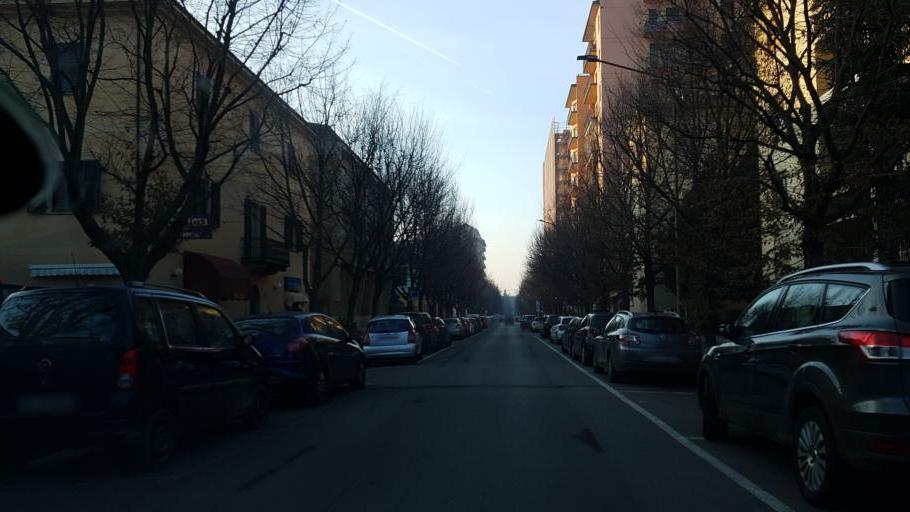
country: IT
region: Piedmont
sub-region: Provincia di Alessandria
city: Novi Ligure
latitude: 44.7629
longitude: 8.7946
